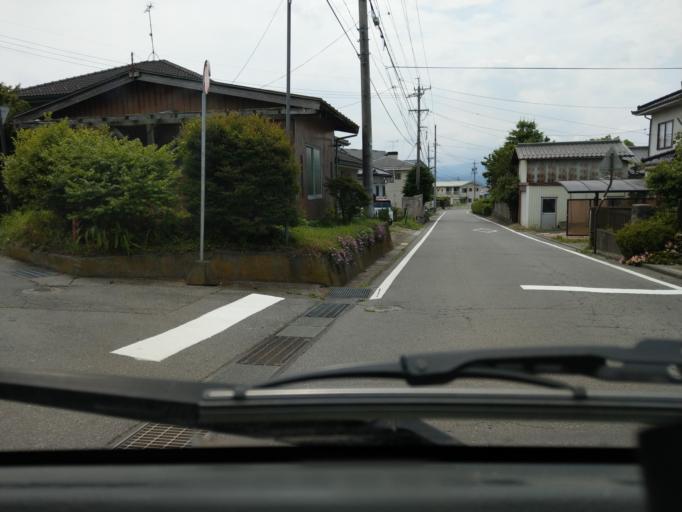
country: JP
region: Nagano
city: Komoro
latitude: 36.3195
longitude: 138.4537
